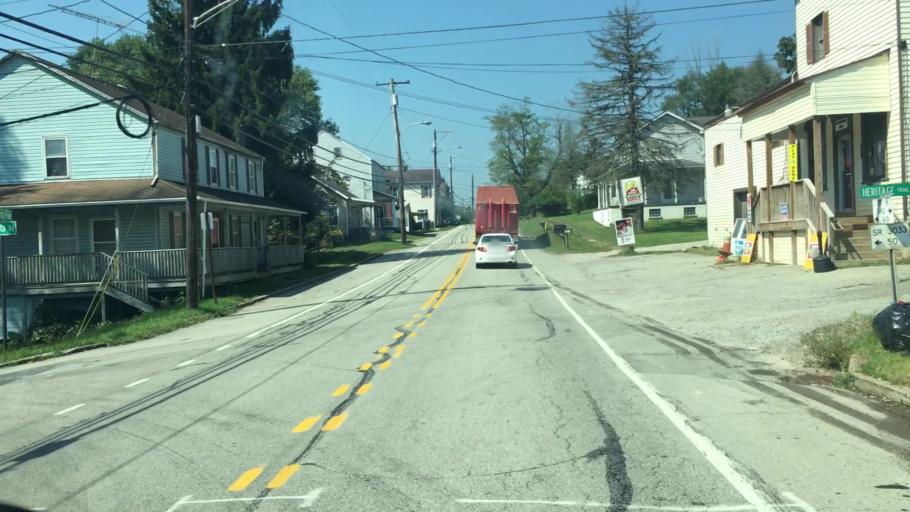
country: US
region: Pennsylvania
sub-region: Washington County
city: Washington
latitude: 40.0463
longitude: -80.2926
